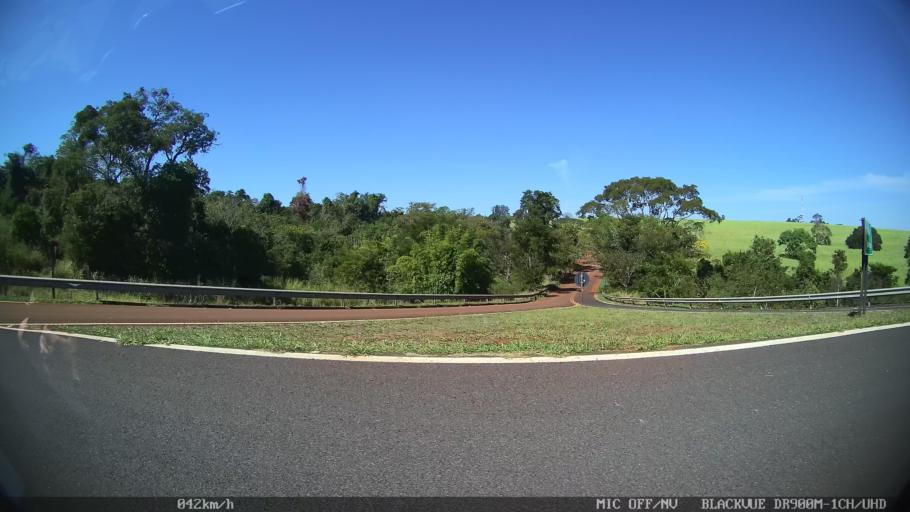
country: BR
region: Sao Paulo
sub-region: Franca
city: Franca
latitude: -20.6338
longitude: -47.4686
